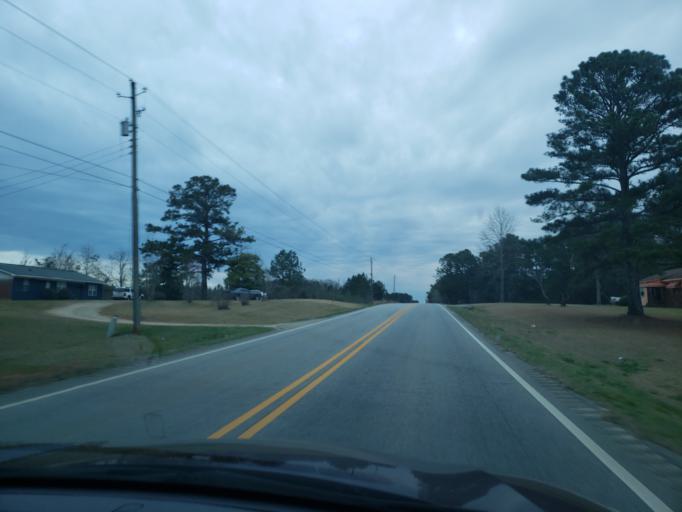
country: US
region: Alabama
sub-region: Chambers County
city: Lafayette
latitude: 32.9980
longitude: -85.3769
